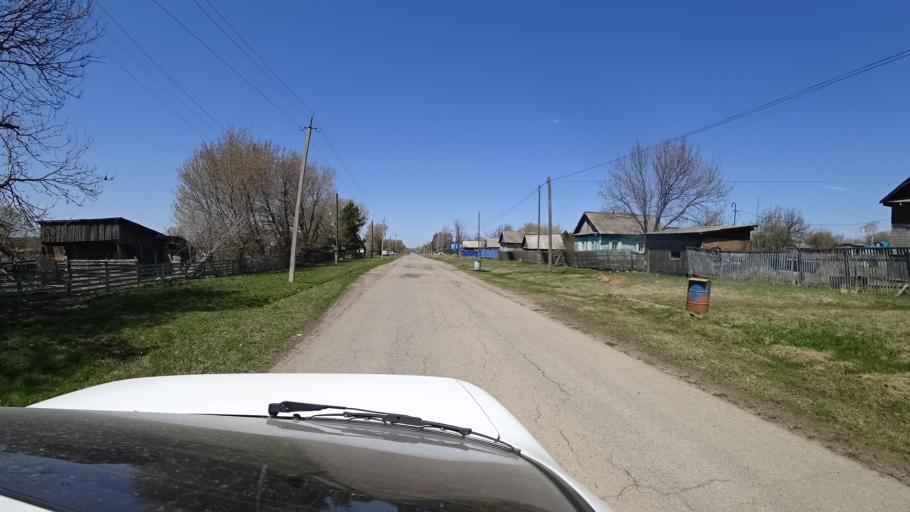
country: RU
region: Primorskiy
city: Lazo
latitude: 45.7920
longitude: 133.7672
